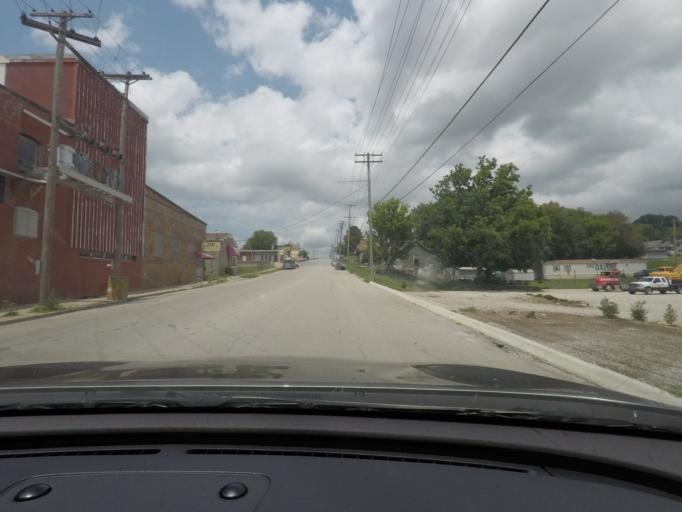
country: US
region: Missouri
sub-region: Carroll County
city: Carrollton
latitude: 39.3529
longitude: -93.4960
